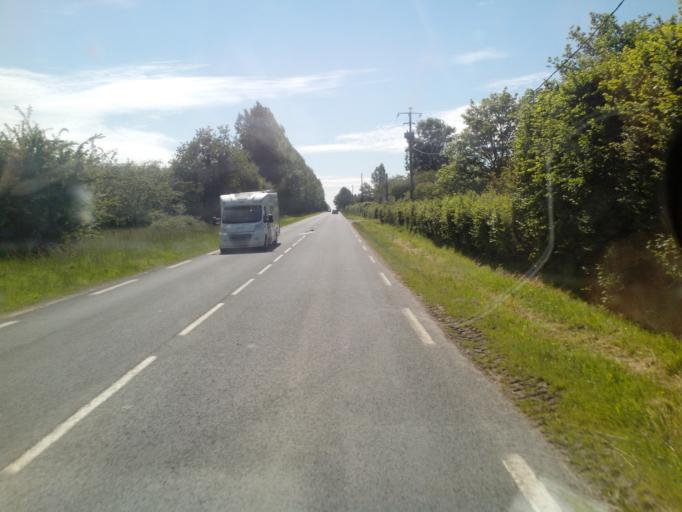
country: FR
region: Haute-Normandie
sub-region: Departement de l'Eure
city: Beuzeville
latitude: 49.3236
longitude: 0.2848
